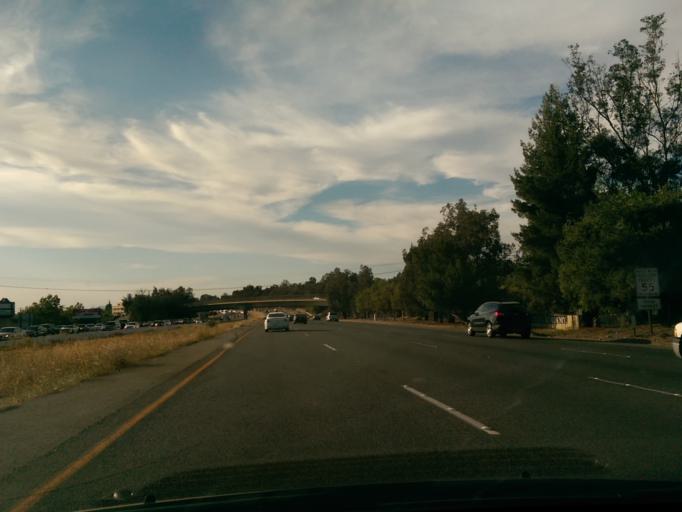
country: US
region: California
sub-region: Riverside County
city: Temecula
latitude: 33.4874
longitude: -117.1431
